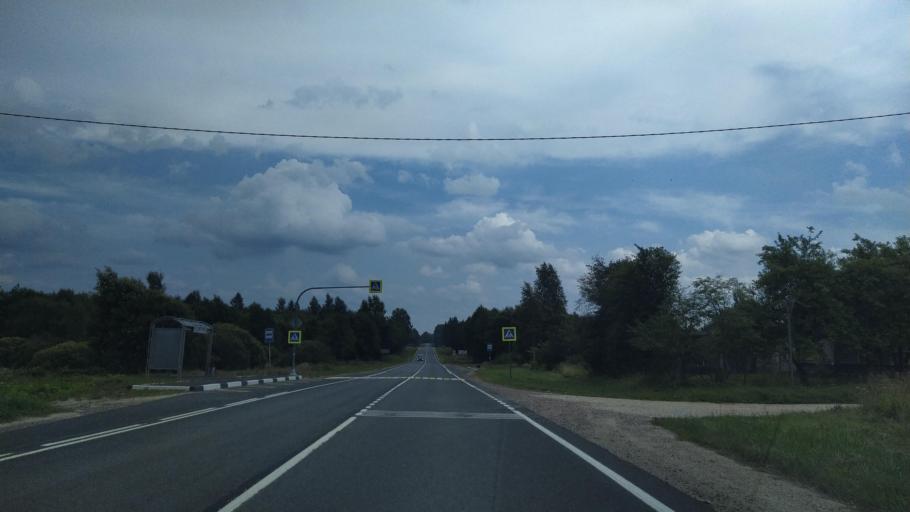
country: RU
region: Pskov
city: Pskov
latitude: 57.8145
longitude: 28.6642
